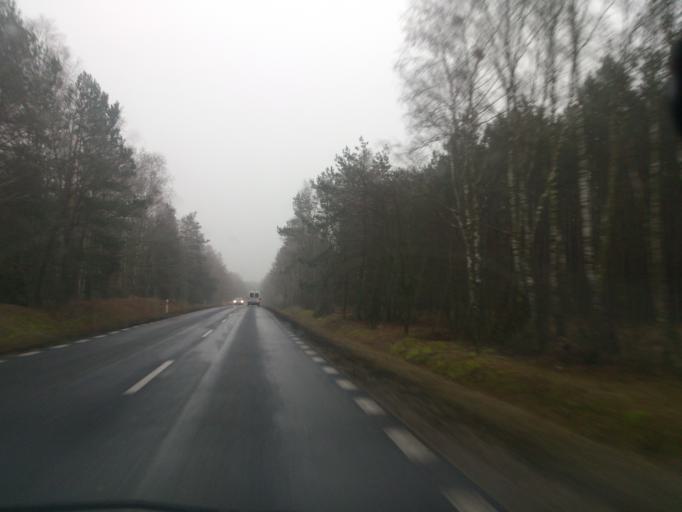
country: PL
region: Masovian Voivodeship
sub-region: Powiat sierpecki
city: Szczutowo
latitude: 52.9234
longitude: 19.6146
